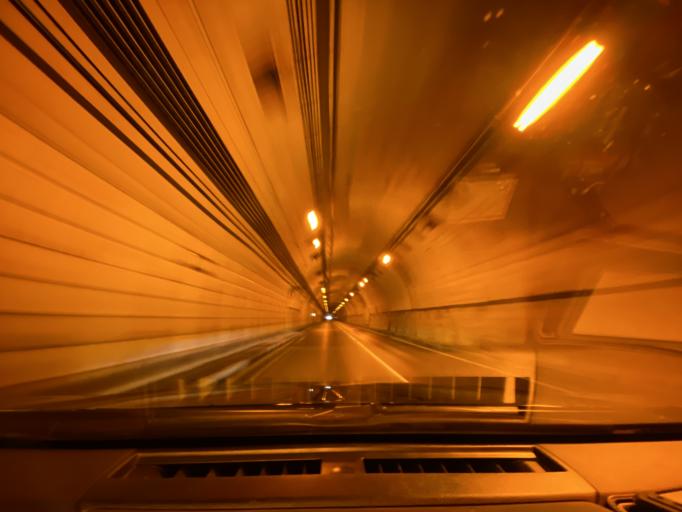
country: JP
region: Hokkaido
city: Rumoi
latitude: 43.7959
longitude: 141.3762
